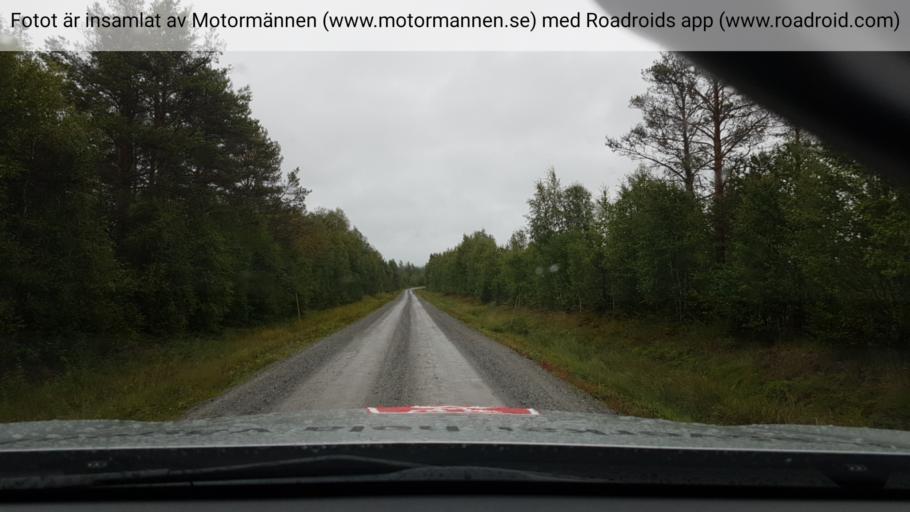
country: SE
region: Vaesterbotten
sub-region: Asele Kommun
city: Asele
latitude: 64.0119
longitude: 17.6234
